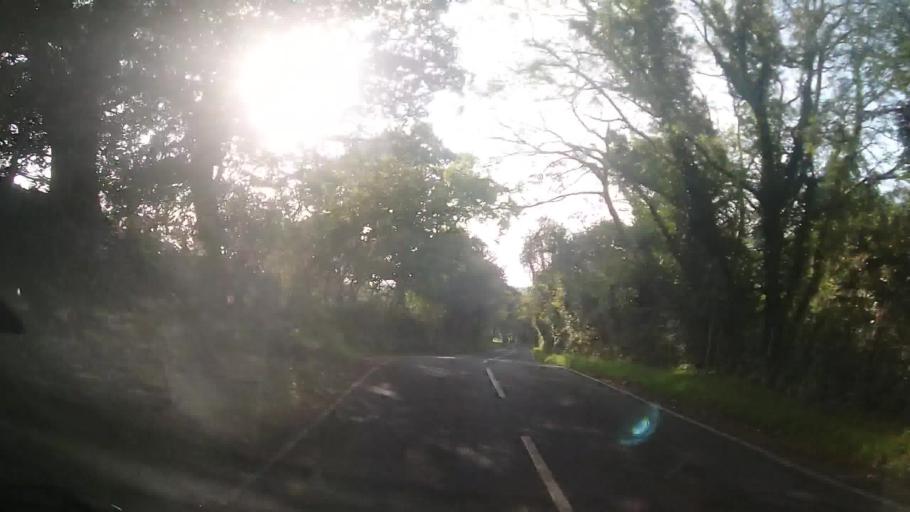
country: GB
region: Wales
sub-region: Pembrokeshire
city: Fishguard
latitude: 51.9773
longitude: -4.9174
